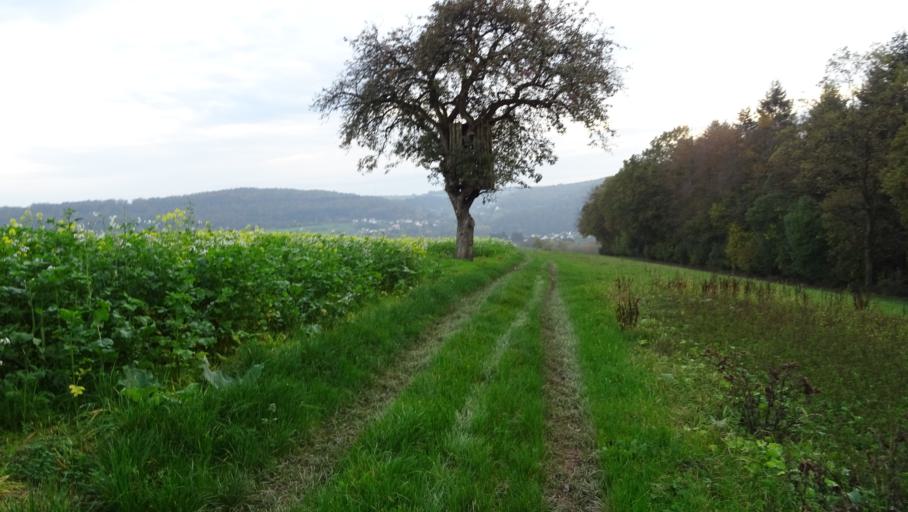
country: DE
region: Baden-Wuerttemberg
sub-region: Karlsruhe Region
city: Binau
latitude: 49.3752
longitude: 9.0698
